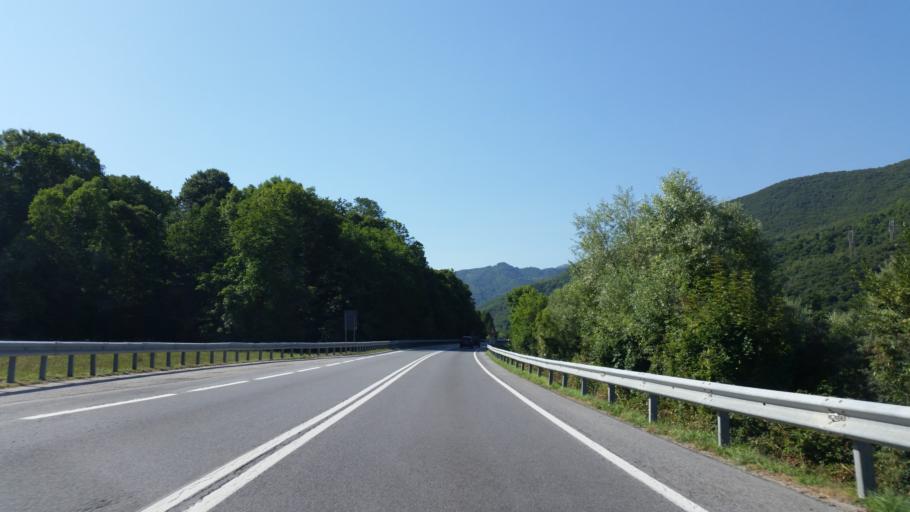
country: IT
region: Piedmont
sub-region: Provincia di Cuneo
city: Robilante
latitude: 44.2865
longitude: 7.5193
